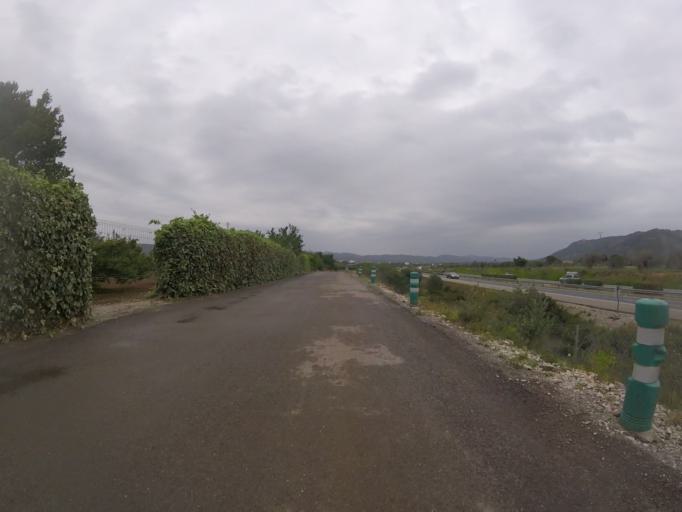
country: ES
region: Valencia
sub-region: Provincia de Castello
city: Alcala de Xivert
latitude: 40.2862
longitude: 0.2279
